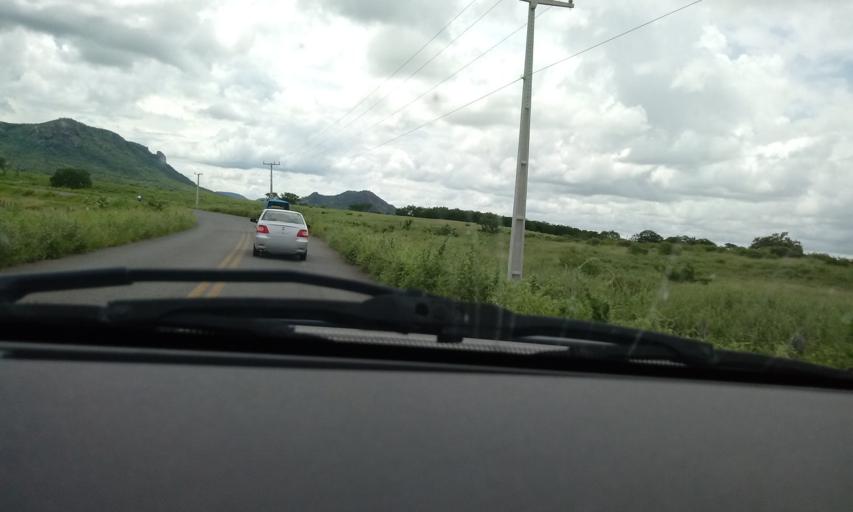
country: BR
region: Bahia
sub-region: Guanambi
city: Guanambi
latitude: -14.1579
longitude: -42.8181
